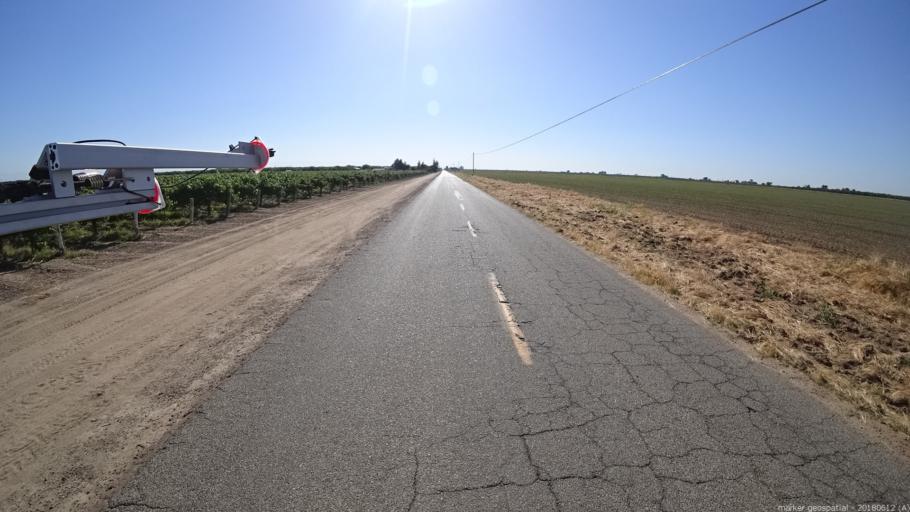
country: US
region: California
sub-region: Madera County
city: Fairmead
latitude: 37.0110
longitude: -120.1643
